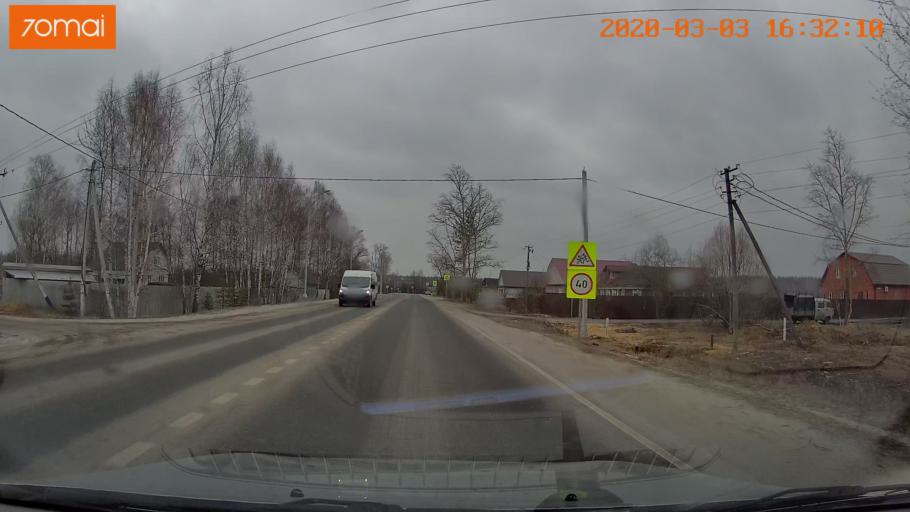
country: RU
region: Moskovskaya
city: Konobeyevo
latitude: 55.4219
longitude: 38.7311
